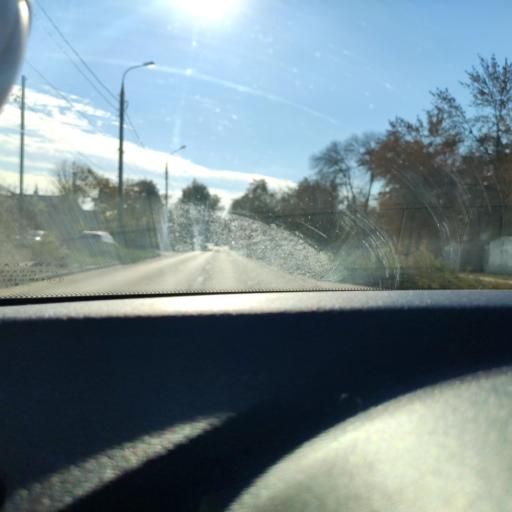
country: RU
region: Samara
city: Smyshlyayevka
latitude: 53.2312
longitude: 50.2988
